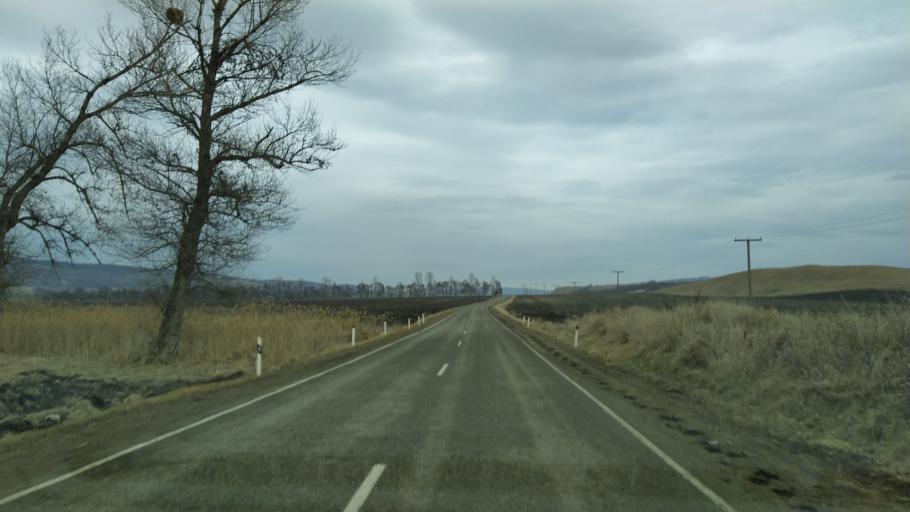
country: RU
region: Krasnodarskiy
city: Peredovaya
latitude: 44.0952
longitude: 41.3923
